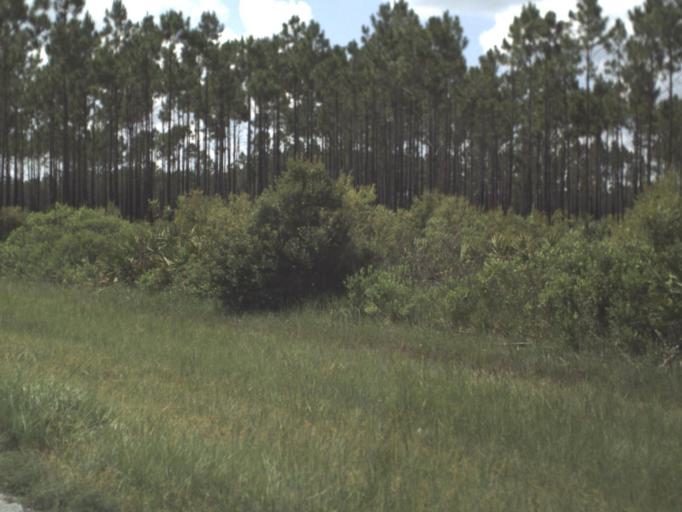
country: US
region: Florida
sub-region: Baker County
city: Macclenny
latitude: 30.5572
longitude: -82.3762
